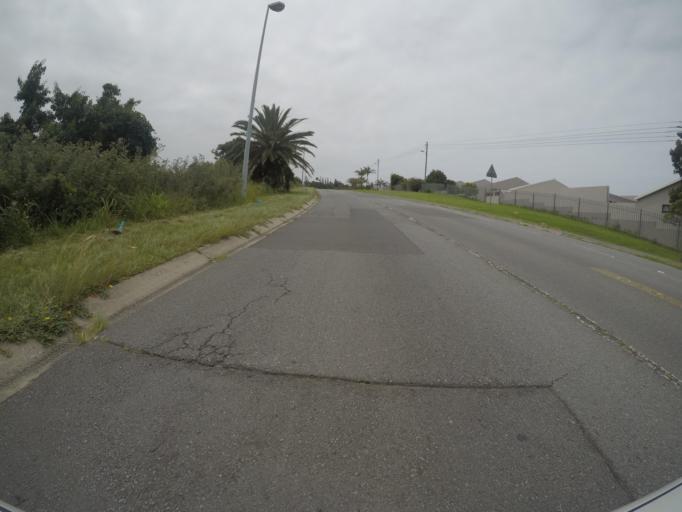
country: ZA
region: Eastern Cape
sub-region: Buffalo City Metropolitan Municipality
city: East London
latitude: -32.9812
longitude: 27.9366
